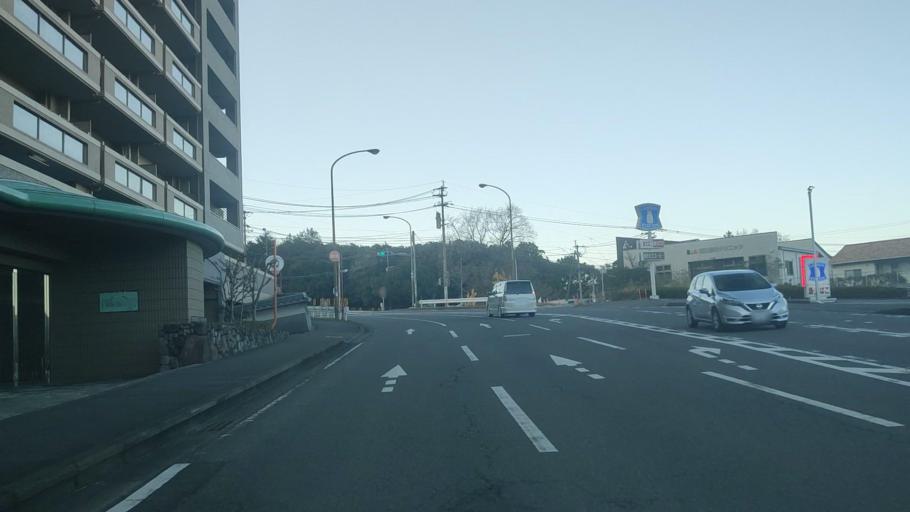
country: JP
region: Oita
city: Beppu
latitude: 33.2841
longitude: 131.4805
